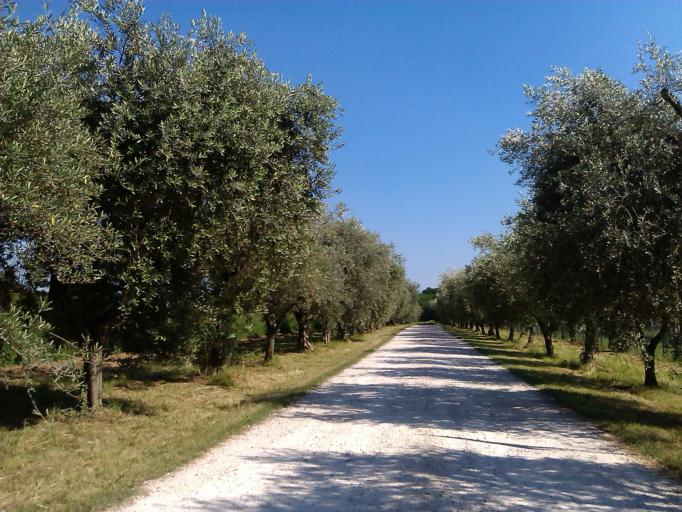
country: IT
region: Veneto
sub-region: Provincia di Vicenza
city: Pove del Grappa
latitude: 45.7860
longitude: 11.7301
